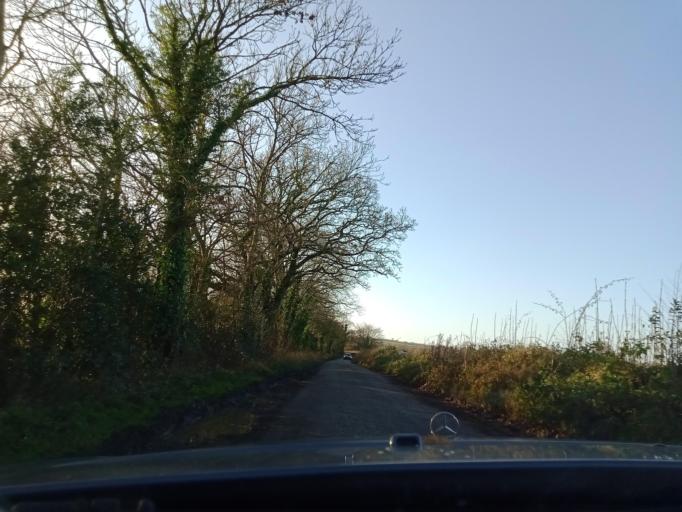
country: IE
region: Leinster
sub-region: Kilkenny
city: Callan
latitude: 52.5031
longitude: -7.3585
